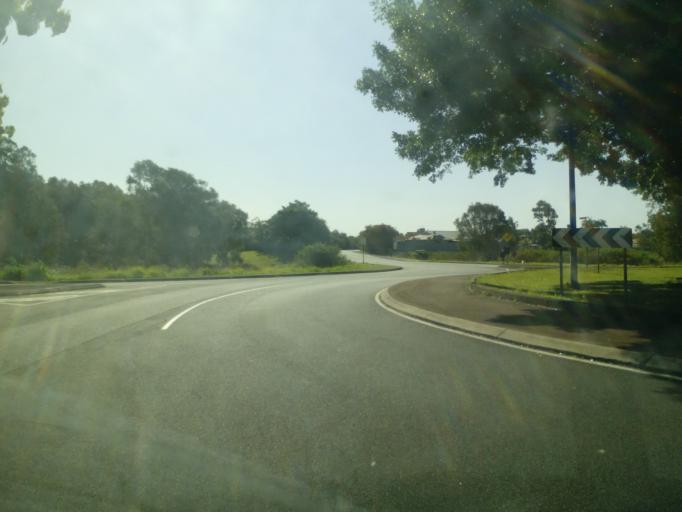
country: AU
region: New South Wales
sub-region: Tweed
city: Kingscliff
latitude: -28.2586
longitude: 153.5702
